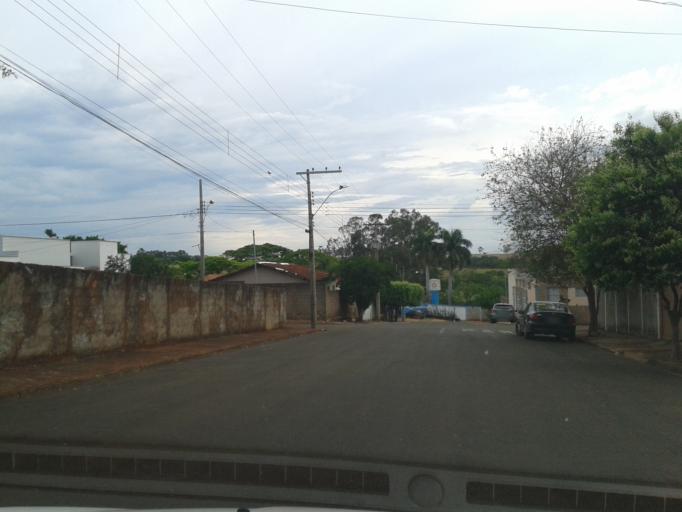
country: BR
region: Minas Gerais
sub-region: Centralina
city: Centralina
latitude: -18.7285
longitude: -49.2039
